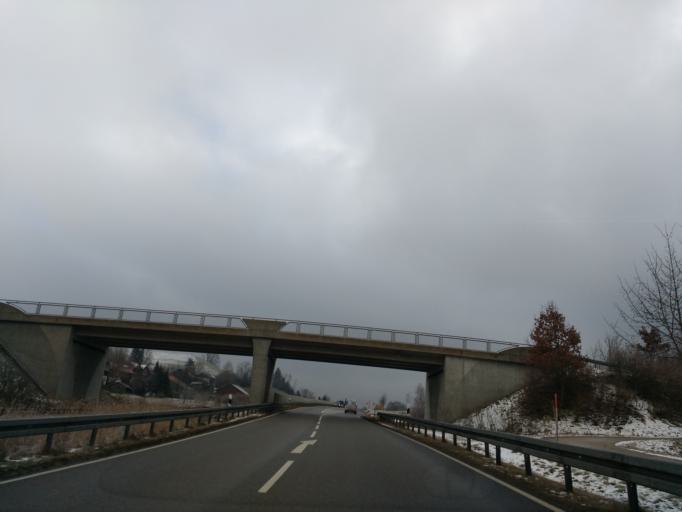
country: DE
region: Bavaria
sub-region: Swabia
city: Nesselwang
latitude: 47.6153
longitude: 10.5170
